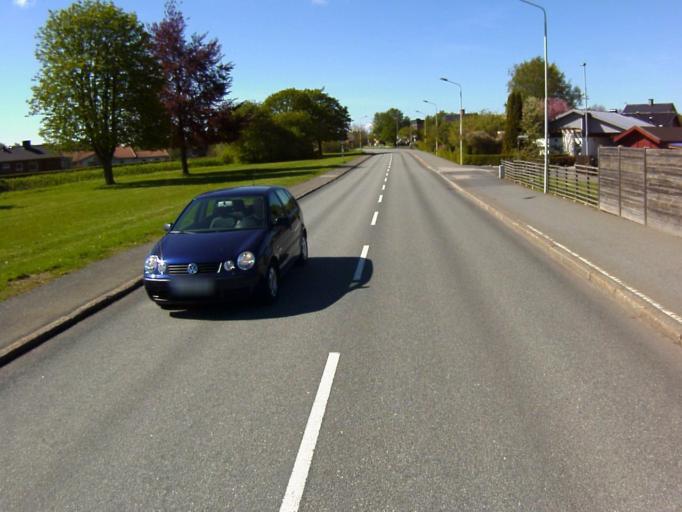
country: SE
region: Skane
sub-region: Kristianstads Kommun
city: Kristianstad
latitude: 56.0493
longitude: 14.1701
